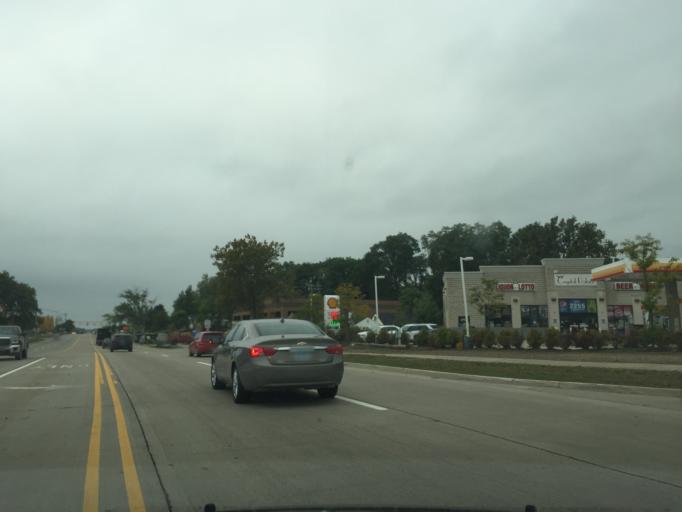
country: US
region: Michigan
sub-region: Oakland County
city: Auburn Hills
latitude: 42.6784
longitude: -83.2462
